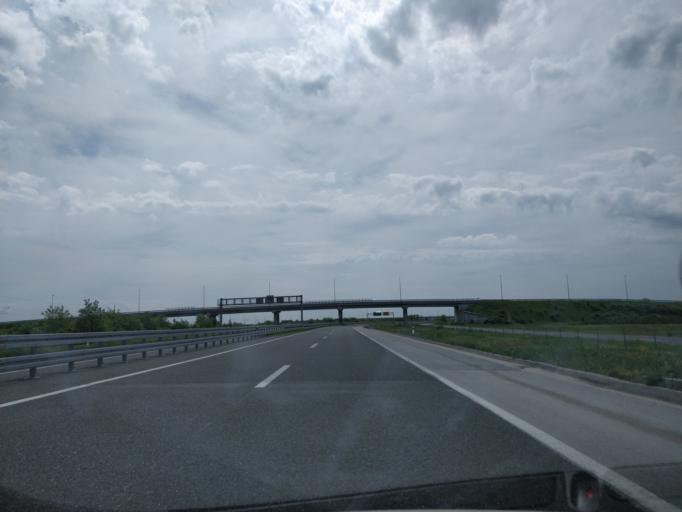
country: HR
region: Zagrebacka
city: Gradici
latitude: 45.6997
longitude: 16.0580
